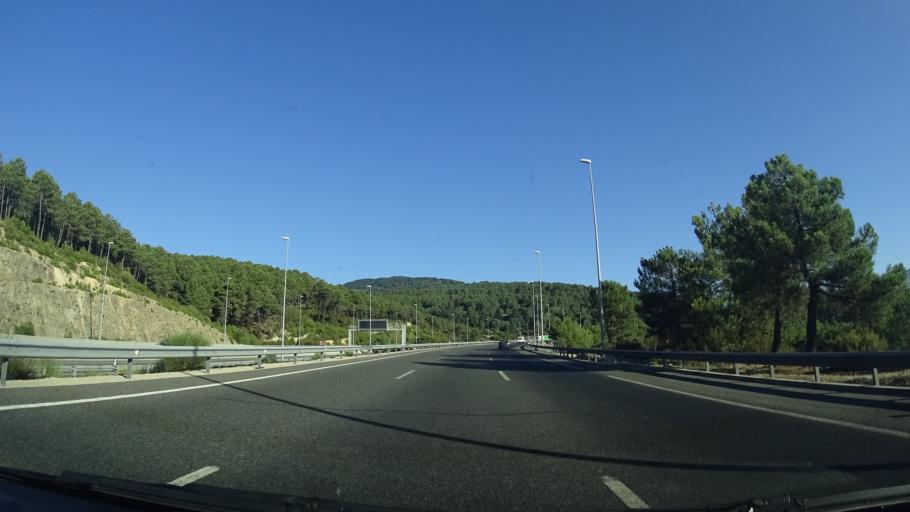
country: ES
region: Madrid
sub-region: Provincia de Madrid
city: Guadarrama
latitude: 40.6772
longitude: -4.1157
